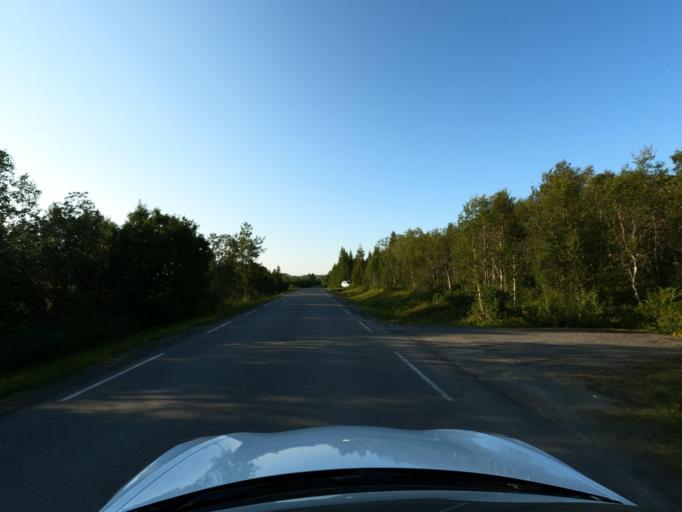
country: NO
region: Troms
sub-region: Skanland
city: Evenskjer
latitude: 68.4830
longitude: 16.7114
